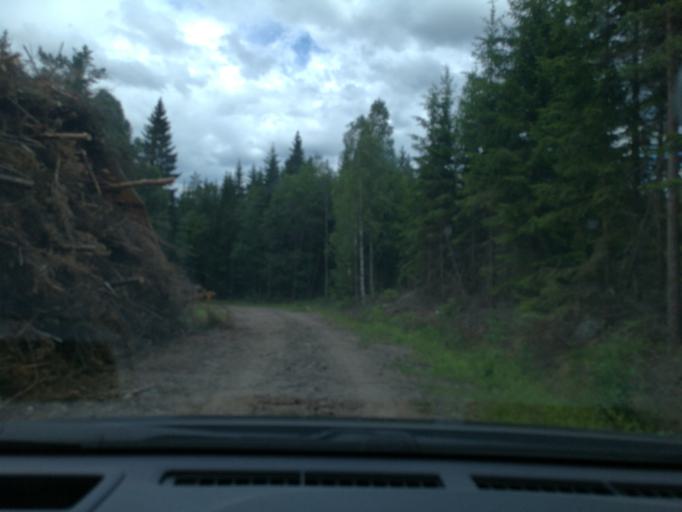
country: SE
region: Vaestmanland
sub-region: Vasteras
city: Skultuna
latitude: 59.8023
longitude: 16.3312
